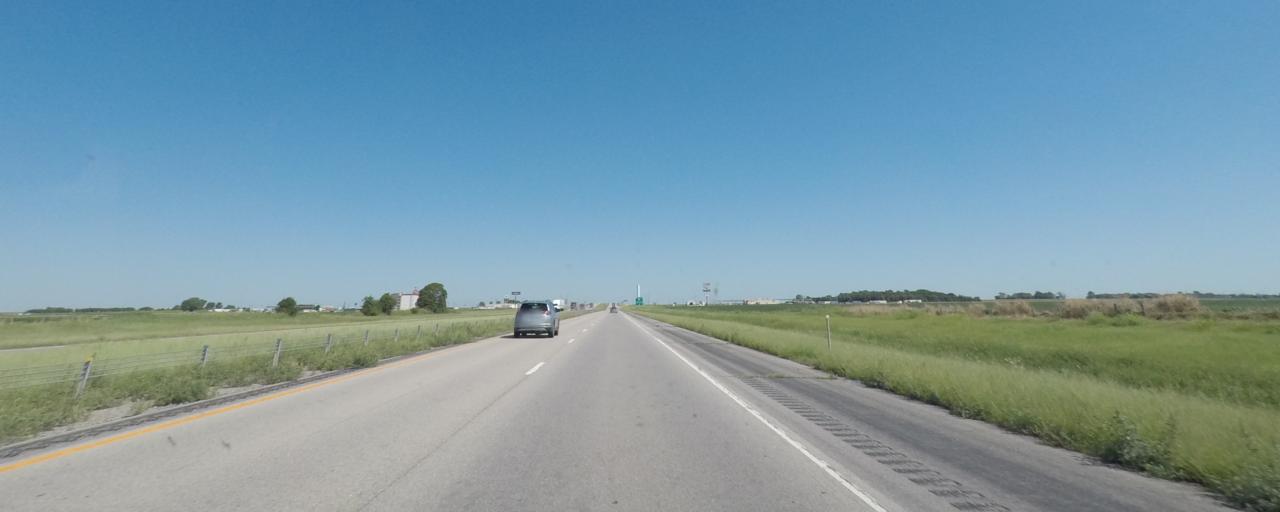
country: US
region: Oklahoma
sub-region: Kay County
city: Tonkawa
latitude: 36.6870
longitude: -97.3457
